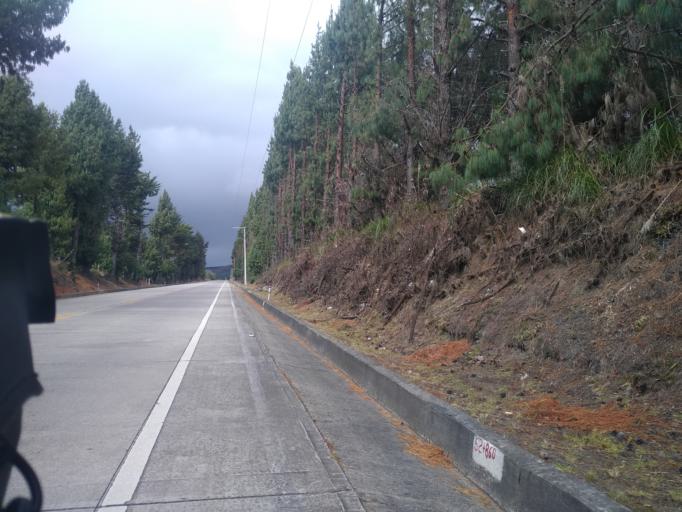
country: EC
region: Azuay
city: Cuenca
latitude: -3.3515
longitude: -79.1857
